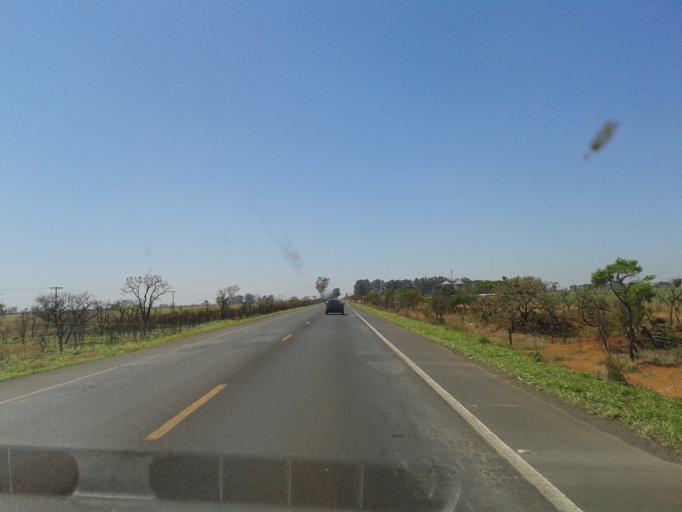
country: BR
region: Minas Gerais
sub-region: Uberaba
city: Uberaba
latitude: -19.3063
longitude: -47.5827
